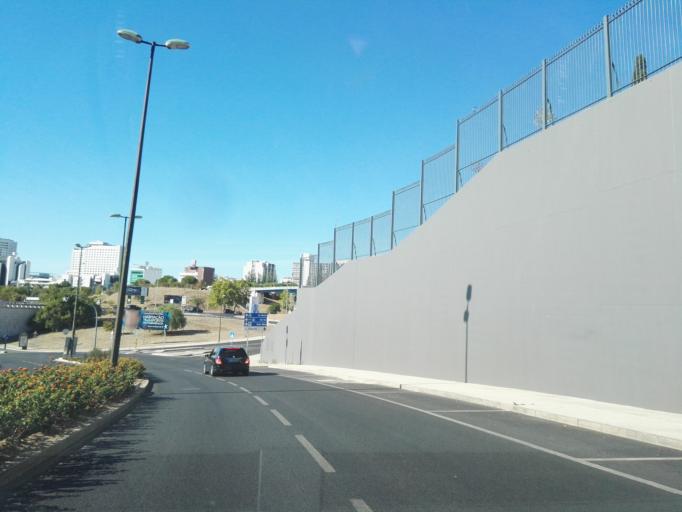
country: PT
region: Lisbon
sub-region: Lisbon
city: Lisbon
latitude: 38.7329
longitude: -9.1628
